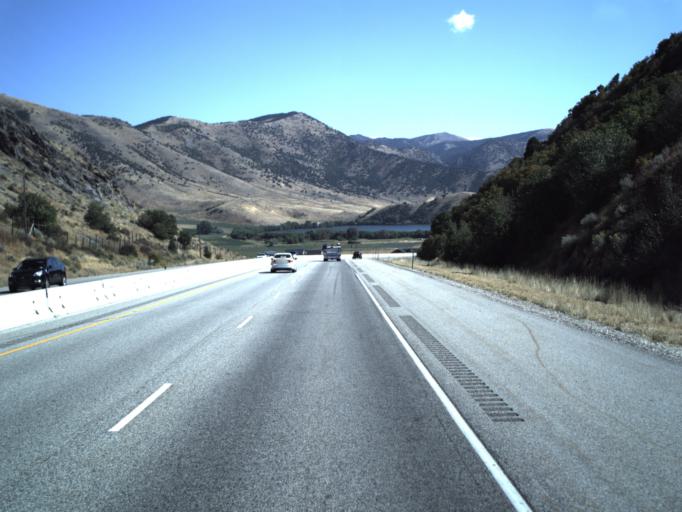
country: US
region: Utah
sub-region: Box Elder County
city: Brigham City
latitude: 41.5213
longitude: -111.9439
